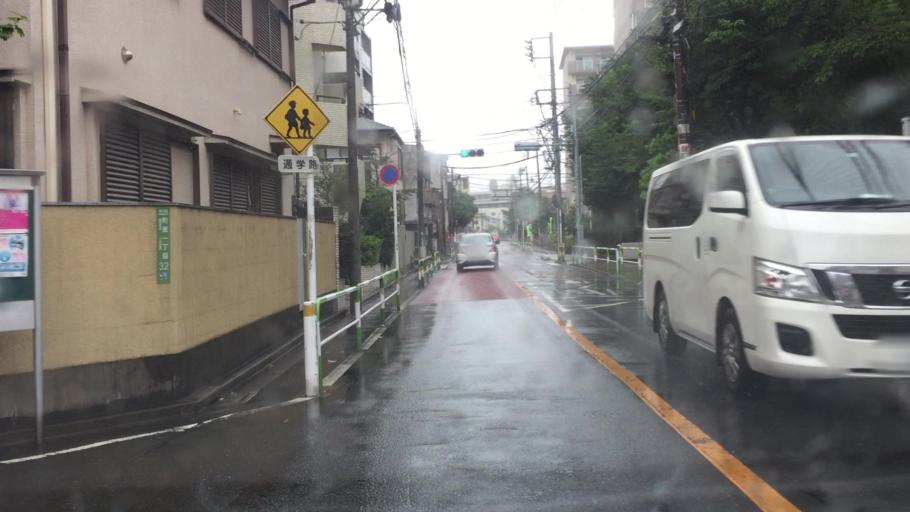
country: JP
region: Saitama
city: Soka
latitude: 35.7462
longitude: 139.7864
